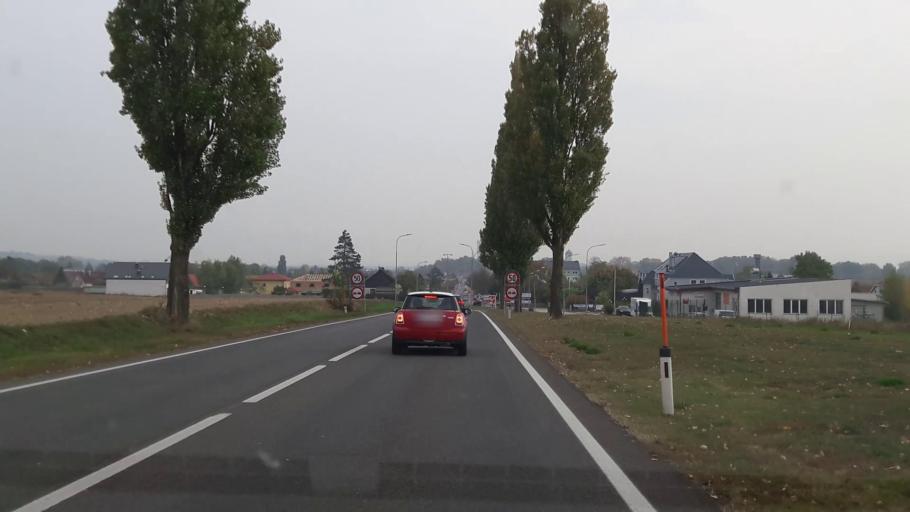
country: AT
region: Lower Austria
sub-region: Politischer Bezirk Wien-Umgebung
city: Schwadorf
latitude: 48.0771
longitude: 16.5740
